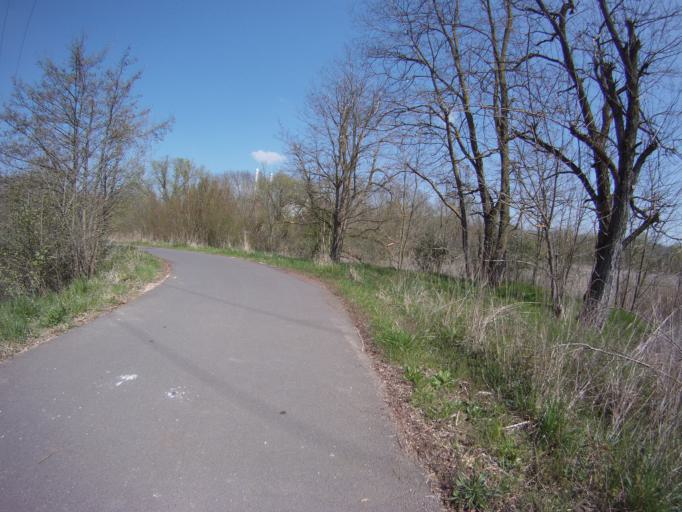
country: FR
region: Lorraine
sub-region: Departement de Meurthe-et-Moselle
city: Dieulouard
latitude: 48.8639
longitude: 6.0750
